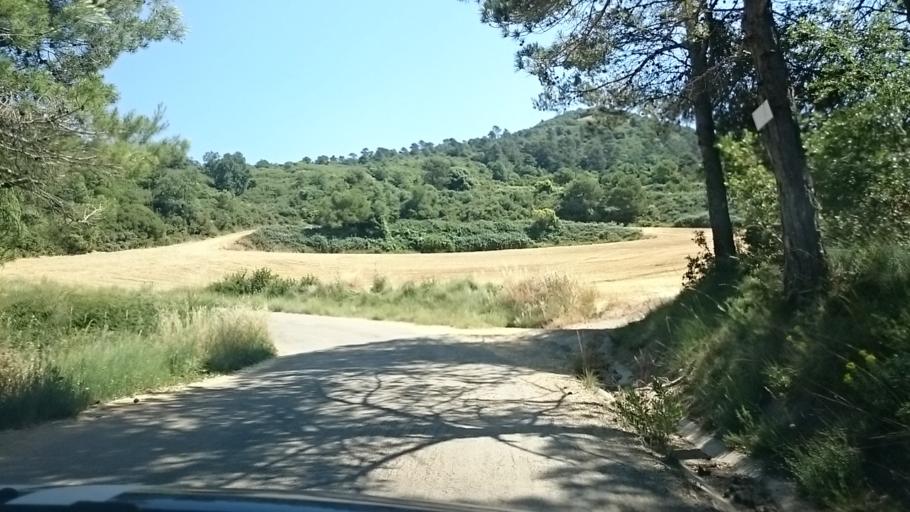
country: ES
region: Catalonia
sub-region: Provincia de Tarragona
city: Querol
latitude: 41.4040
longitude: 1.4174
